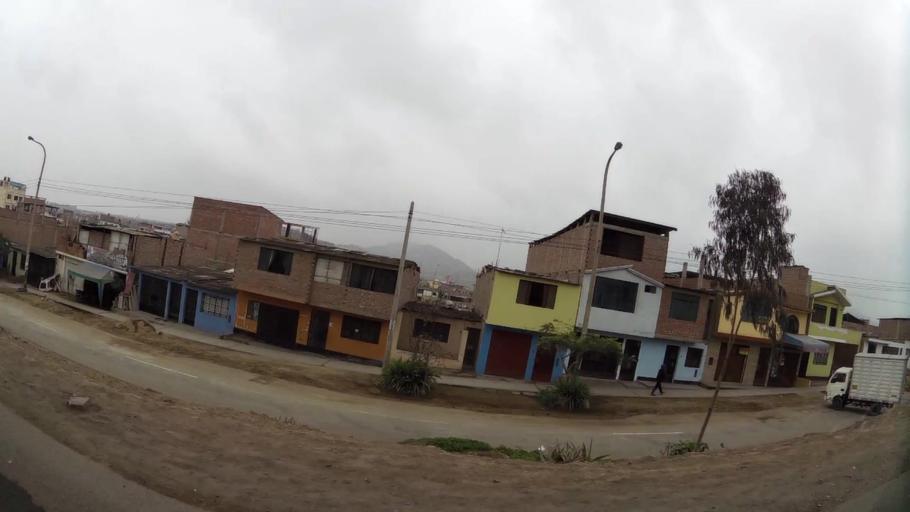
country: PE
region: Lima
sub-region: Lima
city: Punta Hermosa
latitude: -12.2374
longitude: -76.9086
